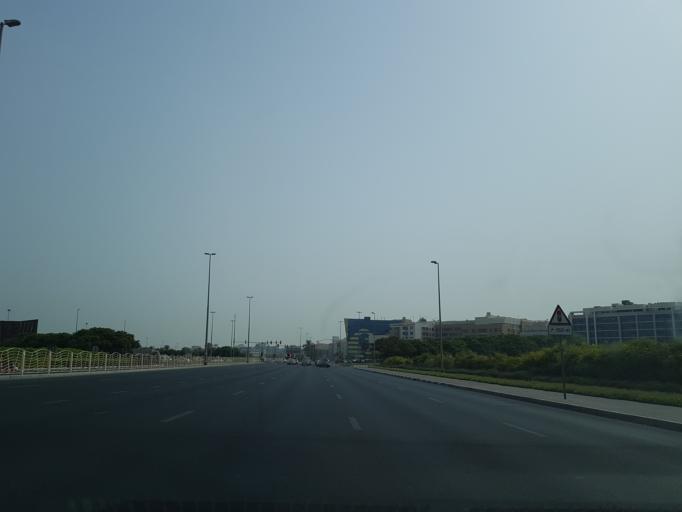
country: AE
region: Ash Shariqah
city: Sharjah
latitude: 25.2483
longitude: 55.2794
